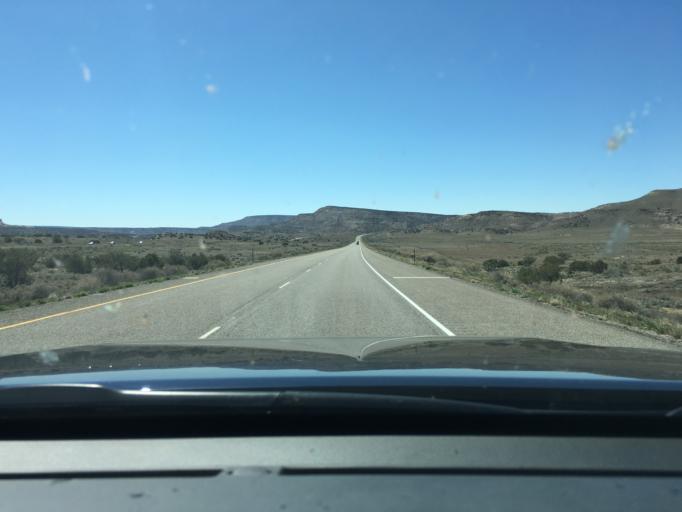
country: US
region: Colorado
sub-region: Mesa County
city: Loma
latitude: 39.2024
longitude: -108.9882
